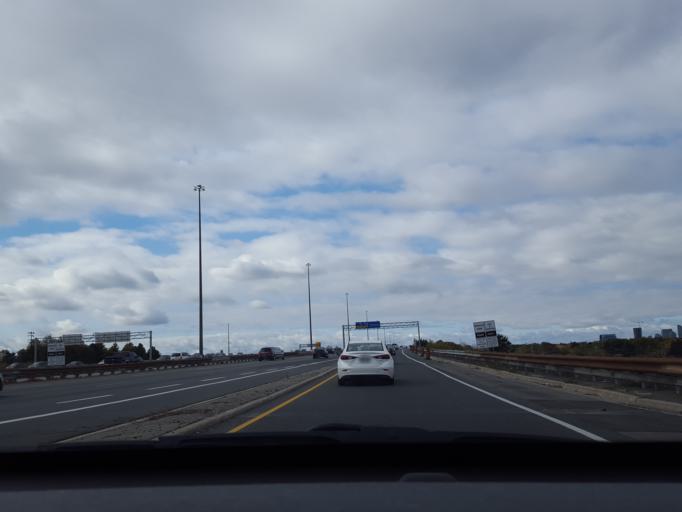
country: CA
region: Ontario
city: Scarborough
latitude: 43.7744
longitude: -79.2883
